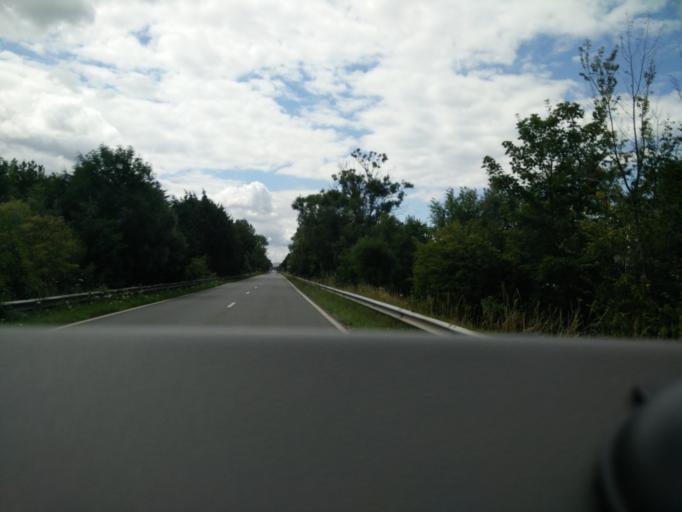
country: FR
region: Nord-Pas-de-Calais
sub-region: Departement du Nord
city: Teteghem
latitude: 51.0388
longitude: 2.4220
